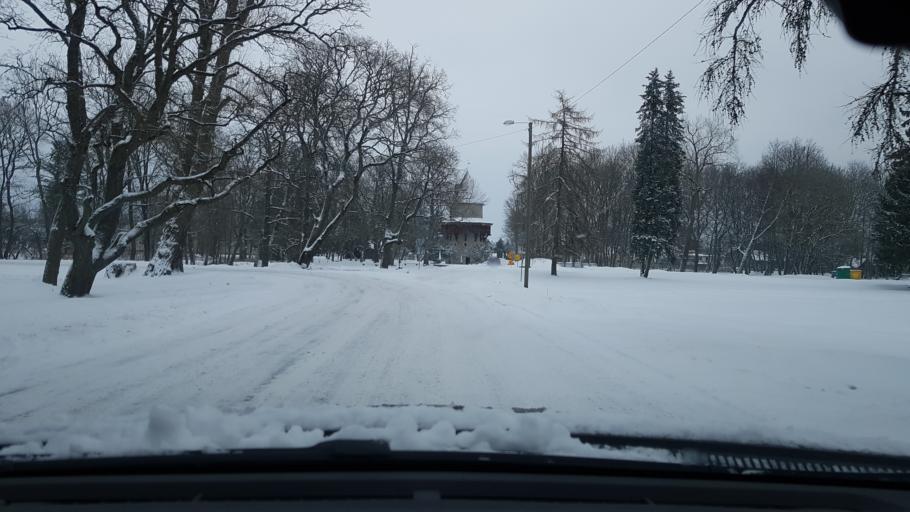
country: EE
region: Harju
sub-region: Kuusalu vald
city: Kuusalu
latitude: 59.4471
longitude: 25.3841
